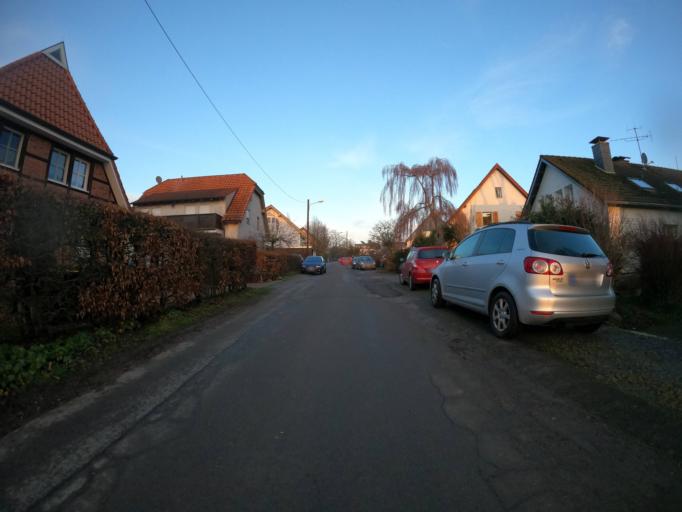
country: DE
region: North Rhine-Westphalia
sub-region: Regierungsbezirk Dusseldorf
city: Solingen
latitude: 51.1769
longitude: 7.1364
